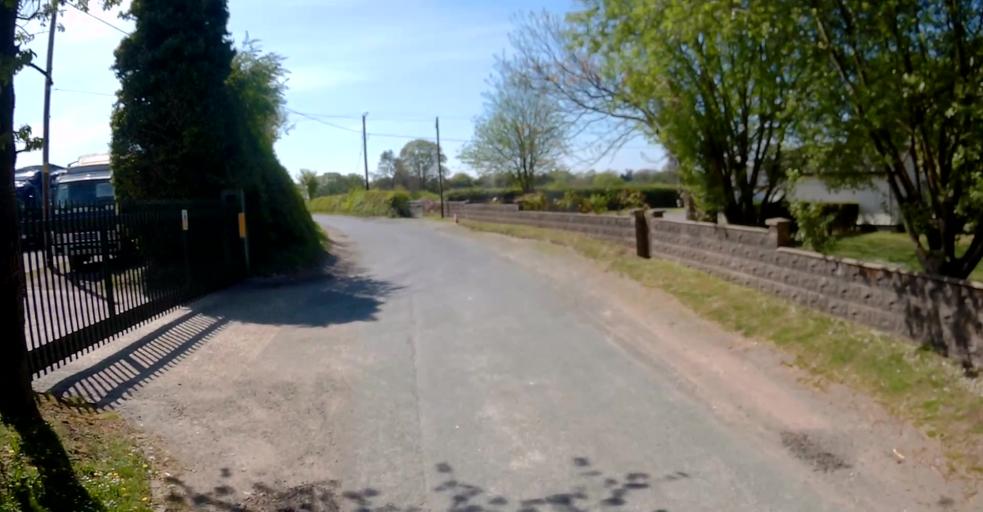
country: GB
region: England
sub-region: Hampshire
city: Overton
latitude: 51.1939
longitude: -1.2473
